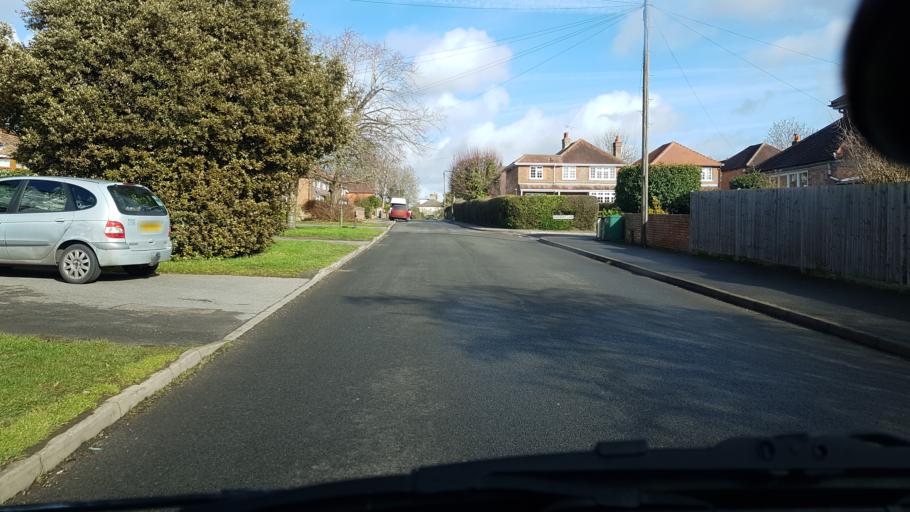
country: GB
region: England
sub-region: Surrey
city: Guildford
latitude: 51.2546
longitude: -0.6012
